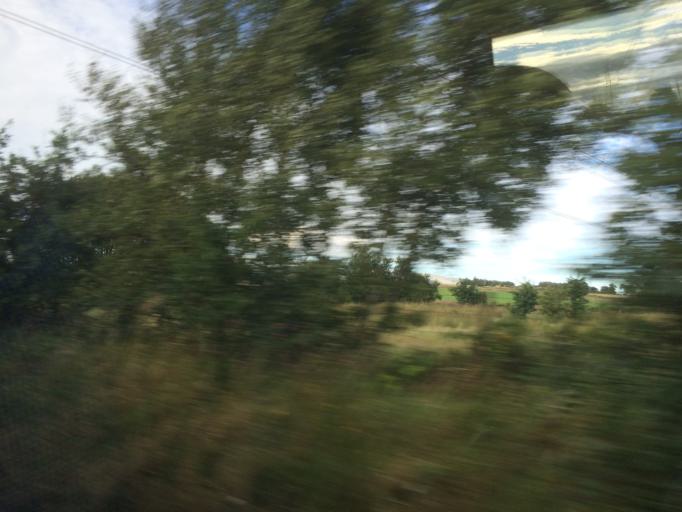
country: GB
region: Scotland
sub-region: Stirling
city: Cowie
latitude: 56.0573
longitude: -3.8491
